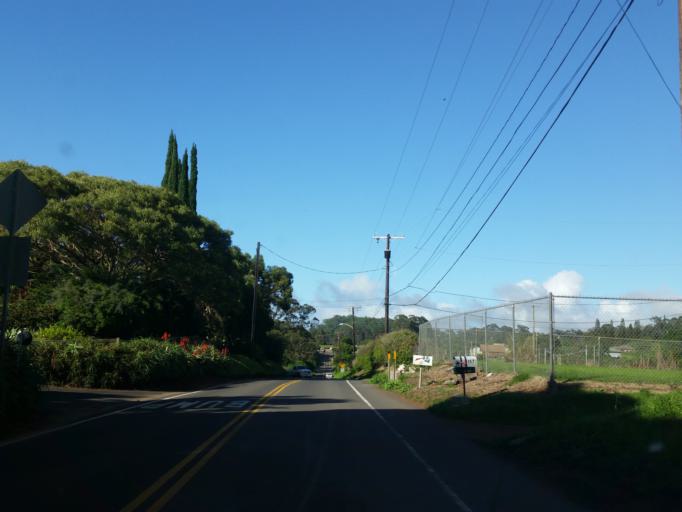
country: US
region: Hawaii
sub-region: Maui County
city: Makawao
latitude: 20.8368
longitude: -156.3106
